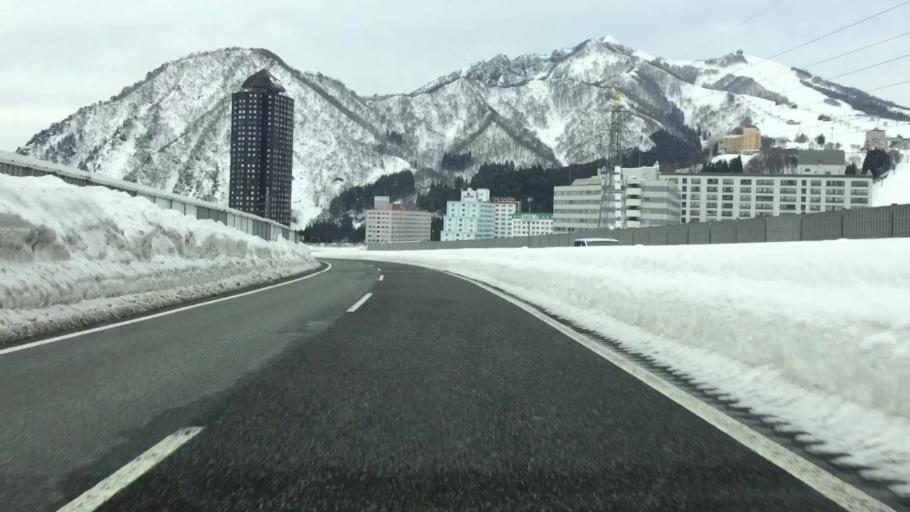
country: JP
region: Niigata
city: Shiozawa
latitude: 36.9261
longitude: 138.8409
